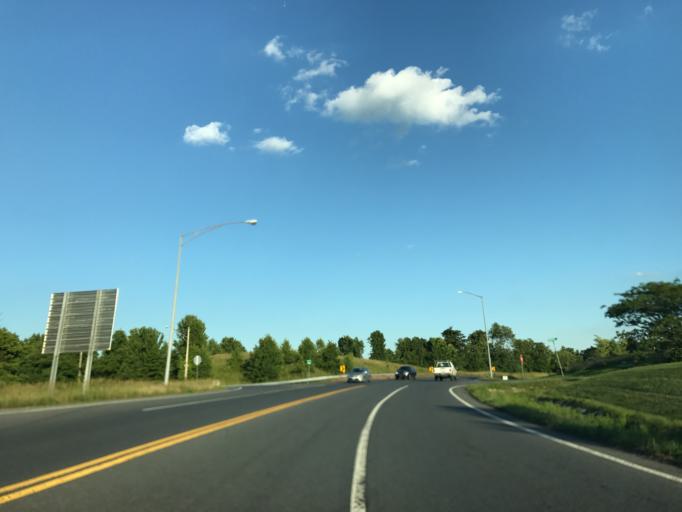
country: US
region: Maryland
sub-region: Anne Arundel County
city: Davidsonville
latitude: 38.9549
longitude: -76.6429
